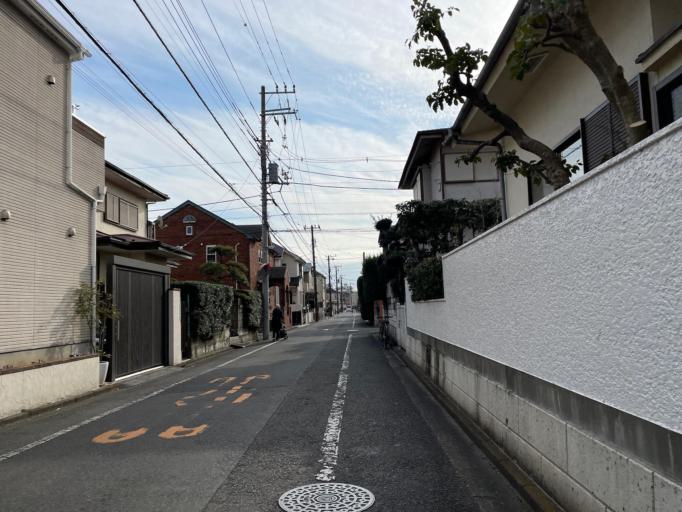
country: JP
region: Tokyo
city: Nishi-Tokyo-shi
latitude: 35.7139
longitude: 139.5369
